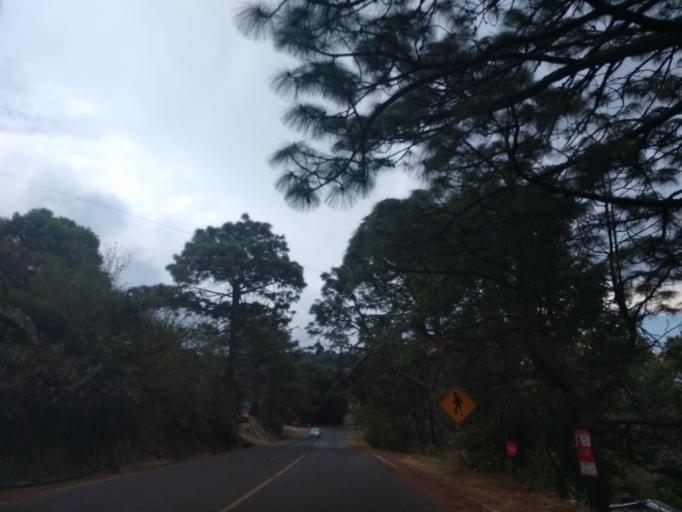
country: MX
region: Jalisco
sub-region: Mazamitla
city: Mazamitla
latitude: 19.9201
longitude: -103.0296
